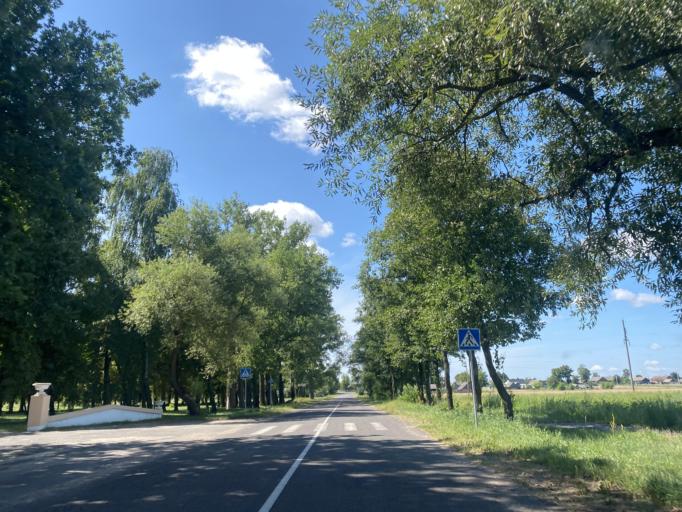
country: BY
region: Brest
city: Ivanava
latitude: 52.2341
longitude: 25.6653
